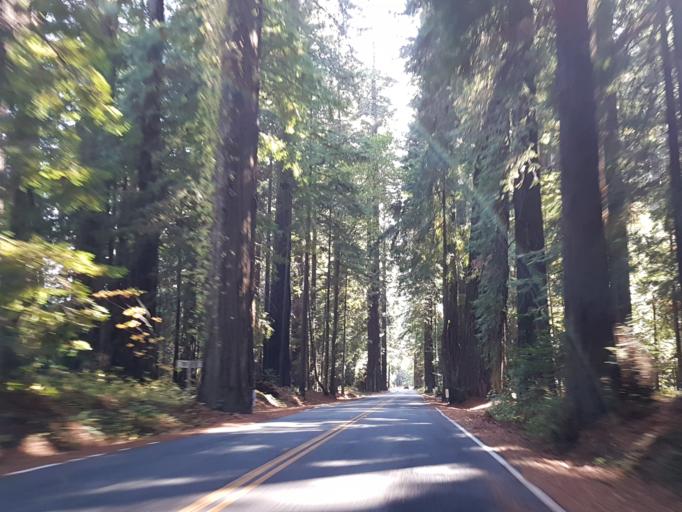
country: US
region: California
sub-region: Humboldt County
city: Rio Dell
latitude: 40.4357
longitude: -123.9851
